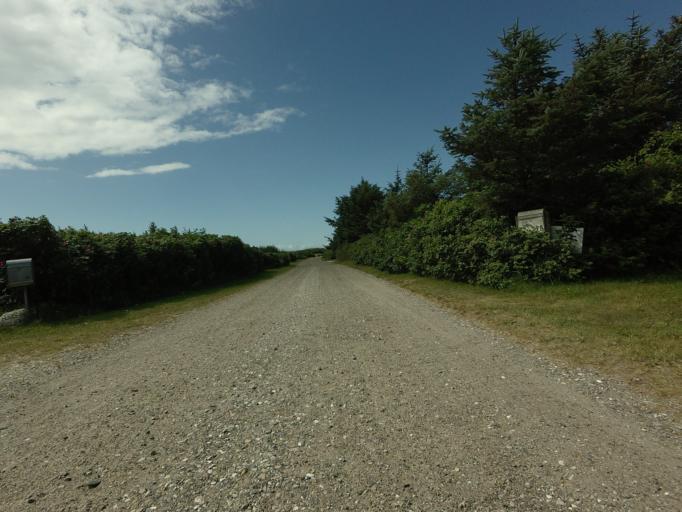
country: DK
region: North Denmark
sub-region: Jammerbugt Kommune
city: Pandrup
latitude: 57.3566
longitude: 9.7015
